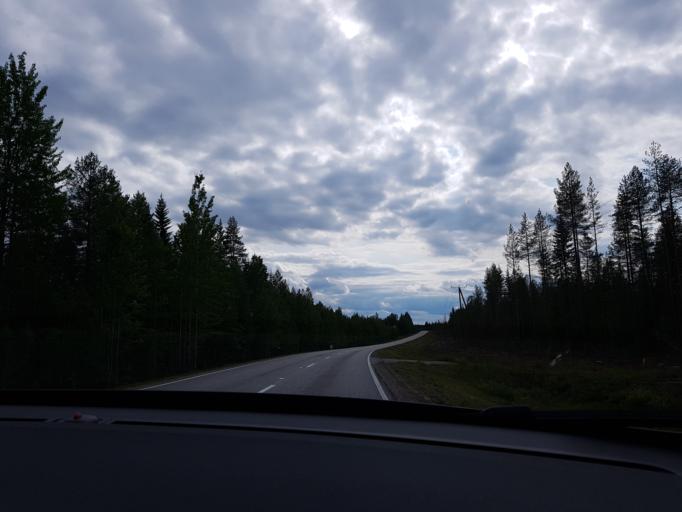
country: FI
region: Kainuu
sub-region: Kehys-Kainuu
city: Kuhmo
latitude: 64.3104
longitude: 29.8669
